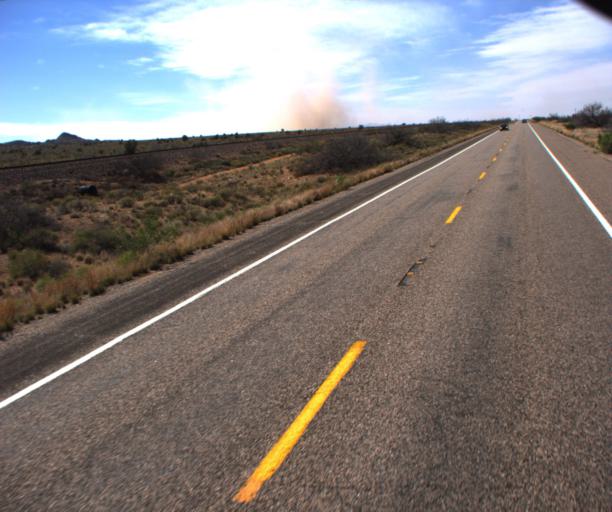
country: US
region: Arizona
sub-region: Mohave County
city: New Kingman-Butler
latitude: 35.4053
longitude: -113.7680
